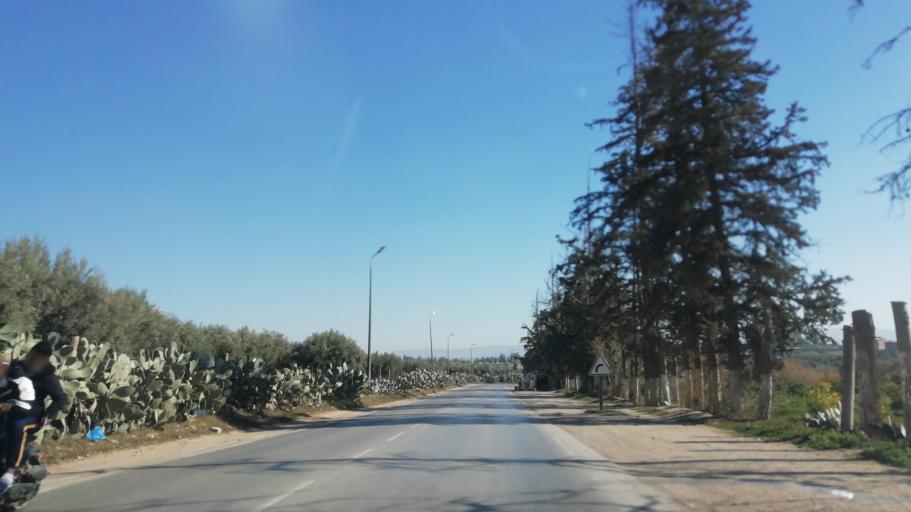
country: DZ
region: Tlemcen
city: Nedroma
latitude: 34.8418
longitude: -1.7139
